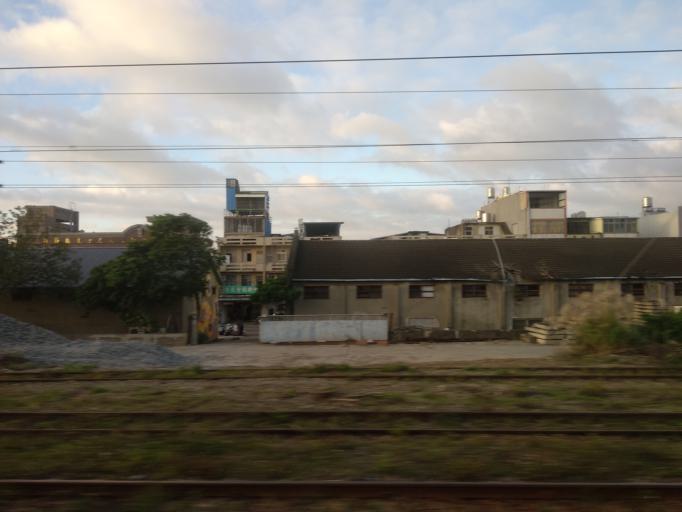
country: TW
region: Taiwan
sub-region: Hsinchu
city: Zhubei
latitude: 24.9344
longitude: 121.0842
